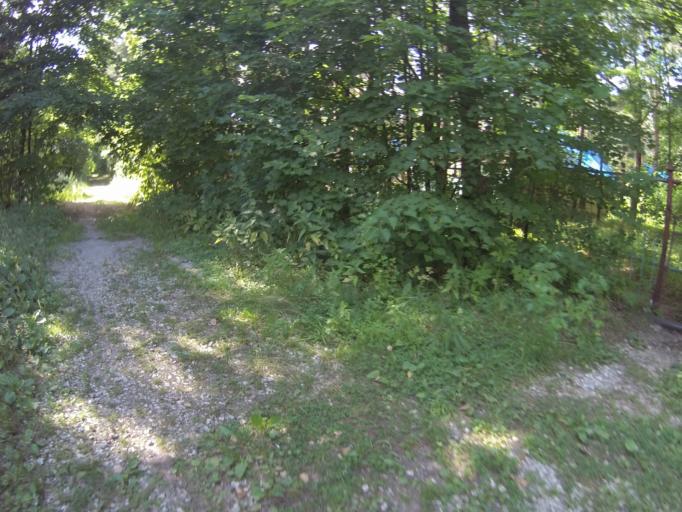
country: RU
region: Vladimir
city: Vorsha
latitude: 56.0416
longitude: 40.2024
